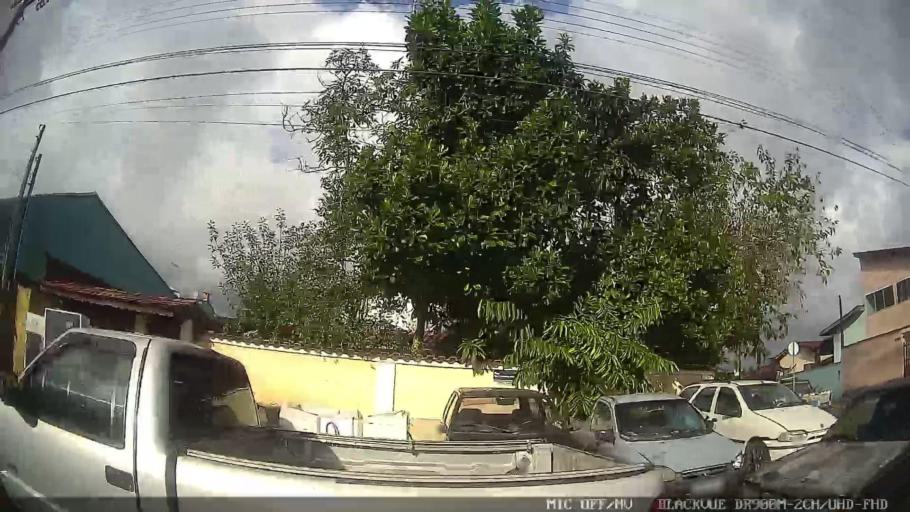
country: BR
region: Sao Paulo
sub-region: Itanhaem
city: Itanhaem
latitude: -24.2174
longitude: -46.8841
